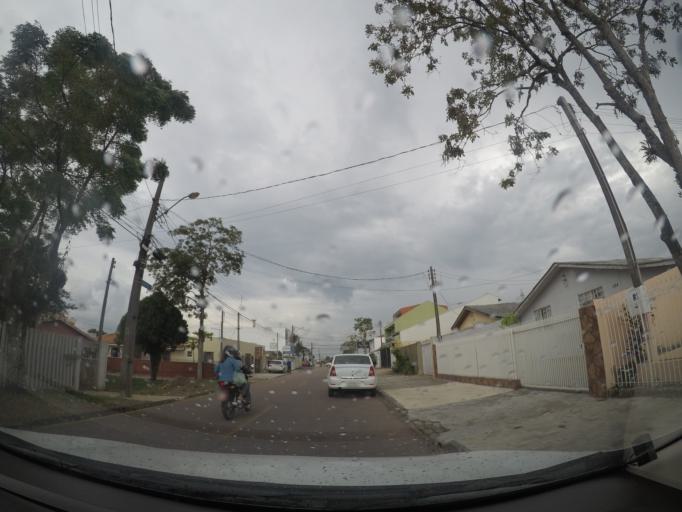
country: BR
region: Parana
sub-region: Sao Jose Dos Pinhais
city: Sao Jose dos Pinhais
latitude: -25.5367
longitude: -49.2771
